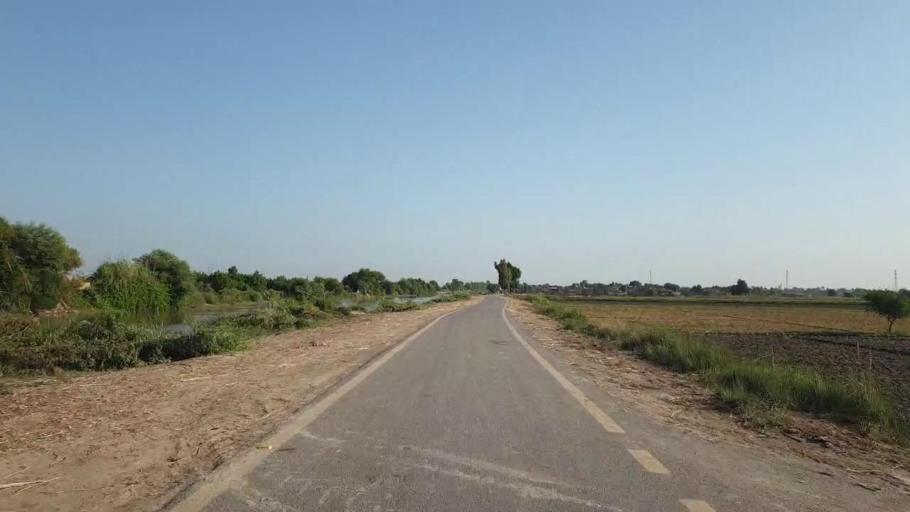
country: PK
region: Sindh
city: Hyderabad
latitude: 25.3277
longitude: 68.4250
